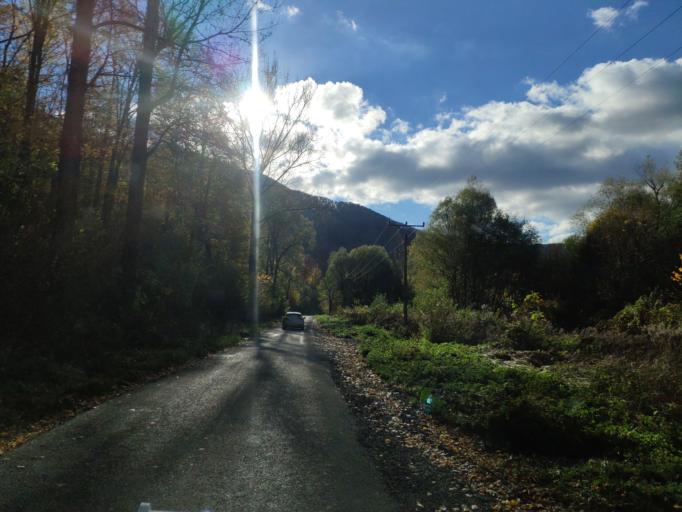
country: SK
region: Presovsky
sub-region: Okres Presov
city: Presov
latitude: 48.8561
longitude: 21.1860
